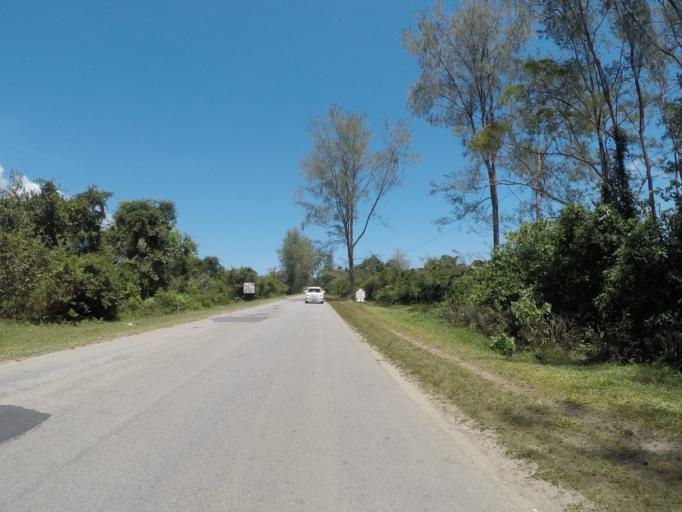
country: TZ
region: Zanzibar Central/South
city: Mahonda
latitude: -6.2787
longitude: 39.4152
